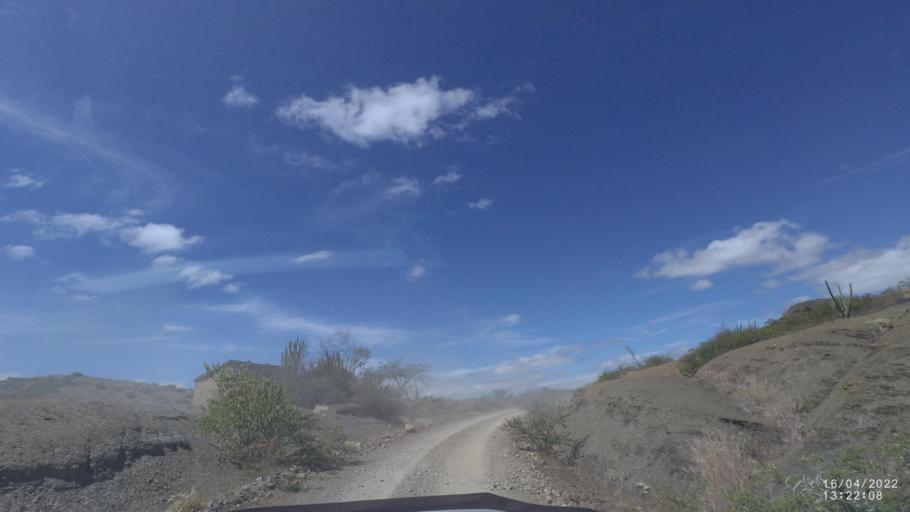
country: BO
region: Cochabamba
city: Mizque
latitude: -17.9919
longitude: -65.6078
